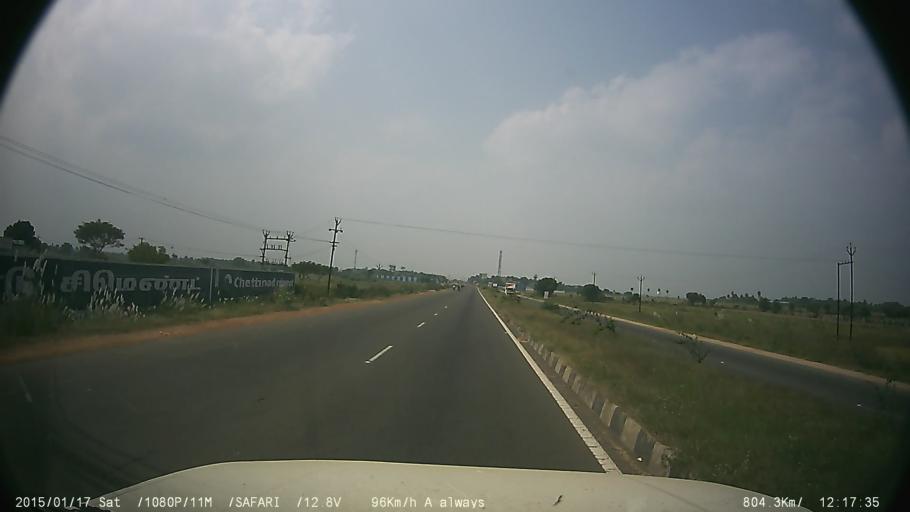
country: IN
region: Tamil Nadu
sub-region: Kancheepuram
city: Sriperumbudur
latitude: 12.9103
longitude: 79.8425
